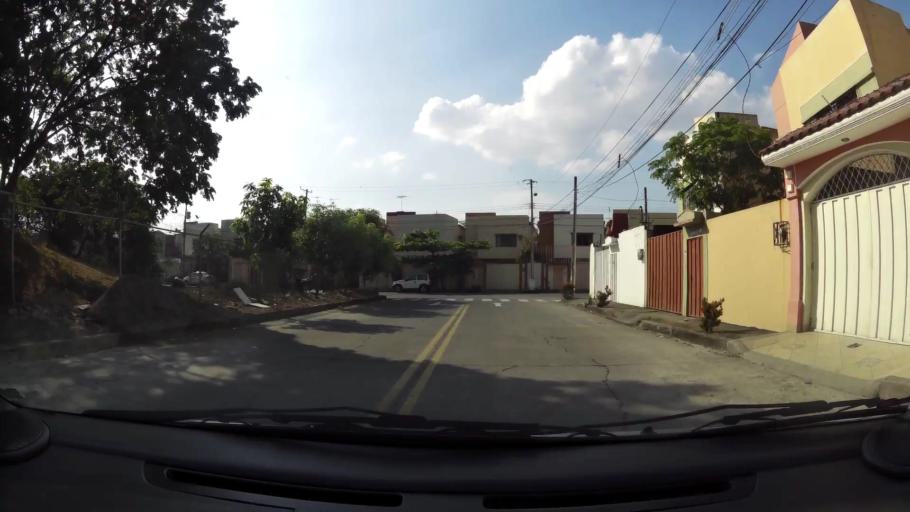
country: EC
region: Guayas
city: Guayaquil
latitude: -2.1390
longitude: -79.9268
